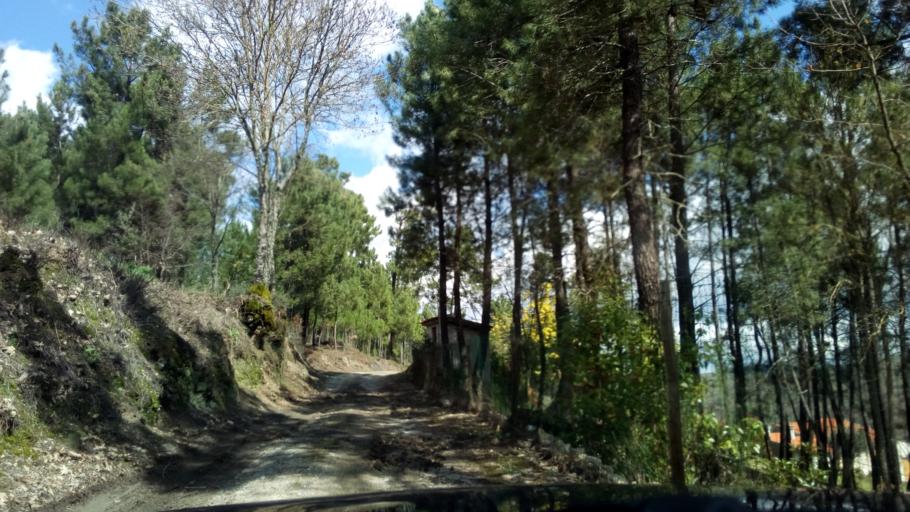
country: PT
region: Guarda
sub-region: Fornos de Algodres
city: Fornos de Algodres
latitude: 40.6265
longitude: -7.5194
